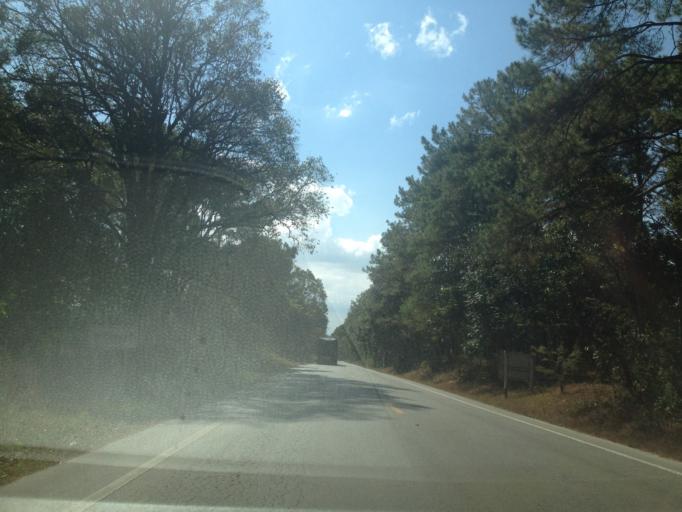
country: TH
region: Chiang Mai
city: Hot
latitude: 18.1443
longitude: 98.3408
